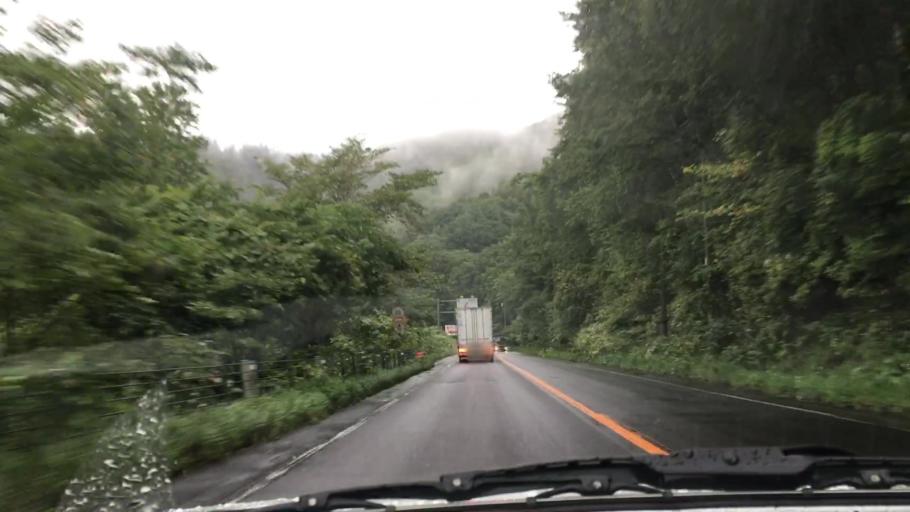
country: JP
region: Hokkaido
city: Niseko Town
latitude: 42.5927
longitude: 140.5918
